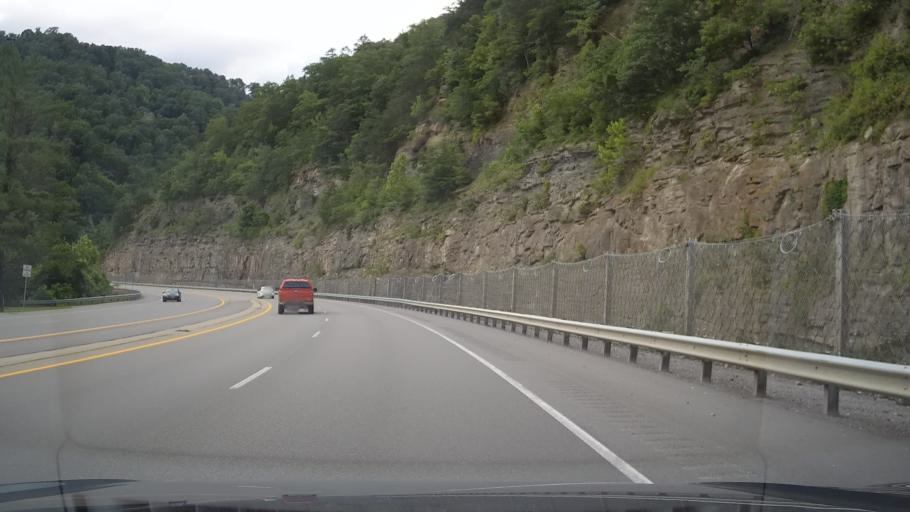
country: US
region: Kentucky
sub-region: Pike County
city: Pikeville
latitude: 37.4477
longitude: -82.5048
